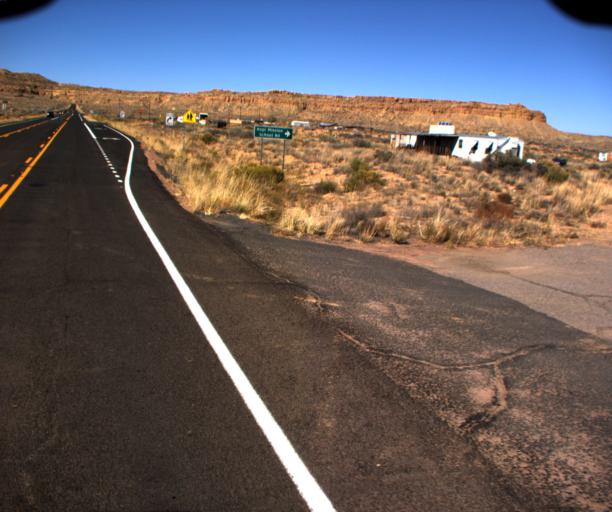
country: US
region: Arizona
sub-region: Navajo County
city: First Mesa
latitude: 35.8771
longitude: -110.6090
